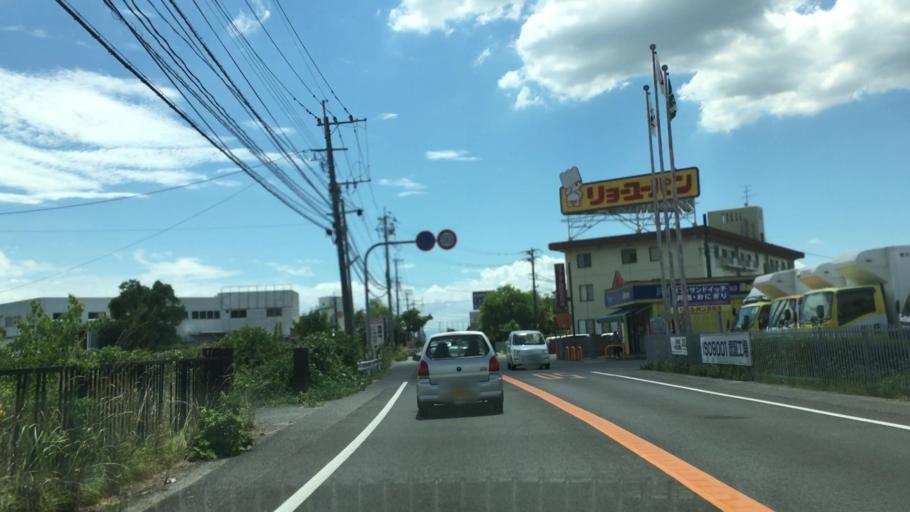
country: JP
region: Saga Prefecture
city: Kanzakimachi-kanzaki
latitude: 33.2851
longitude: 130.3480
